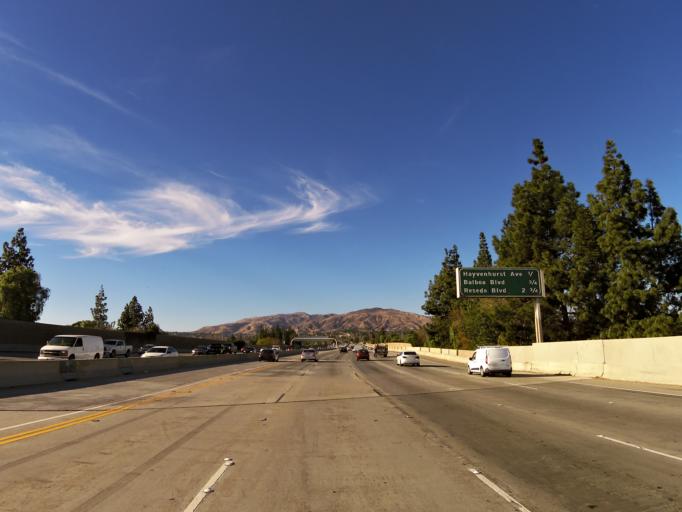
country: US
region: California
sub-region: Los Angeles County
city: San Fernando
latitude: 34.2681
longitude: -118.4850
